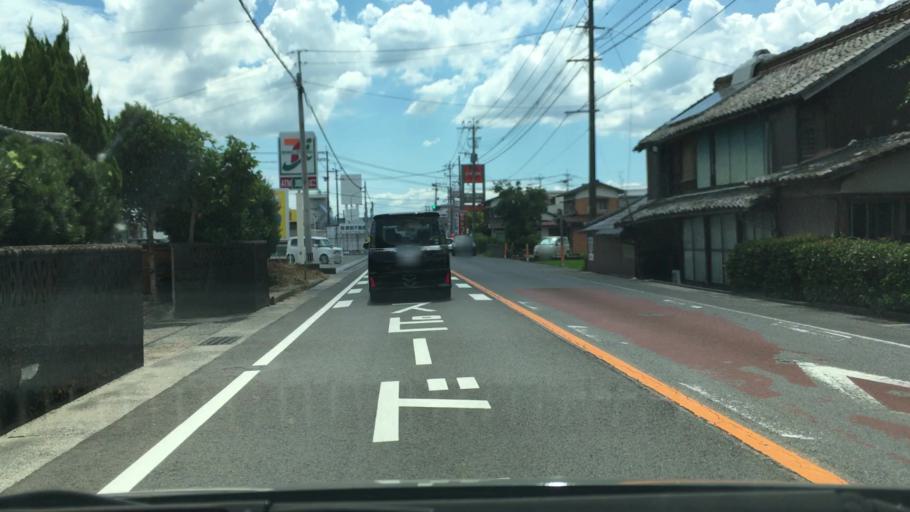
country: JP
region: Saga Prefecture
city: Kanzakimachi-kanzaki
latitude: 33.3333
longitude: 130.4148
